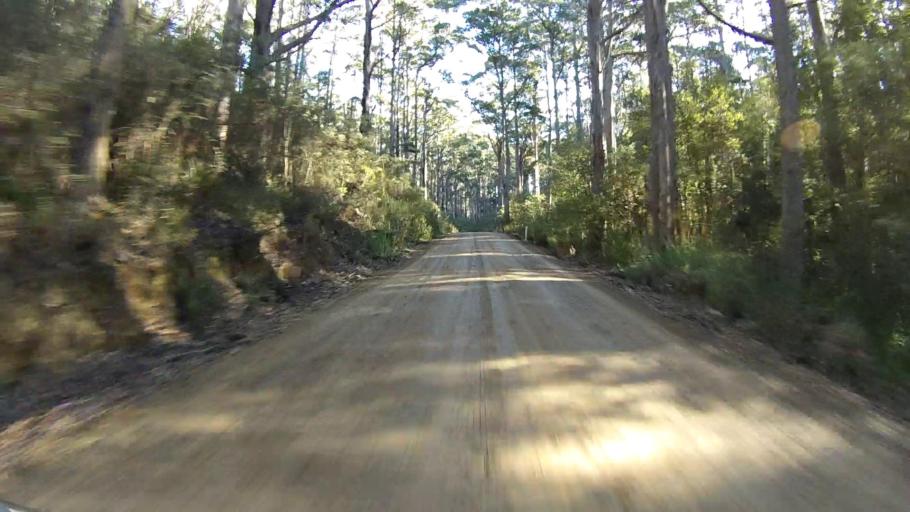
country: AU
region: Tasmania
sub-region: Clarence
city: Sandford
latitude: -43.1450
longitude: 147.9428
